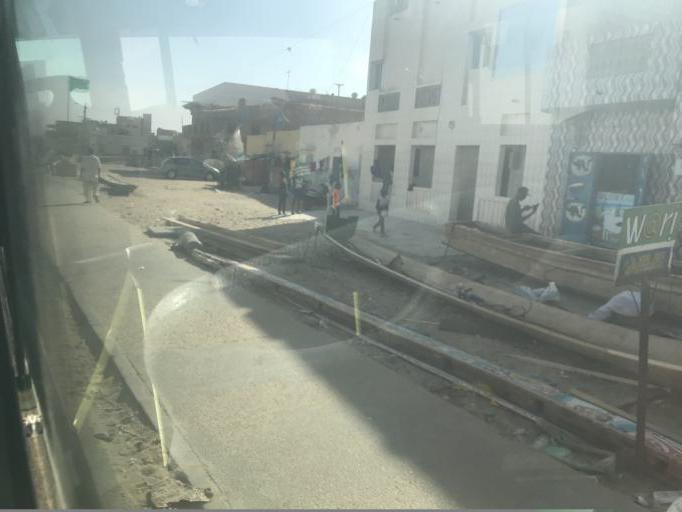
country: SN
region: Saint-Louis
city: Saint-Louis
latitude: 16.0459
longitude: -16.5057
